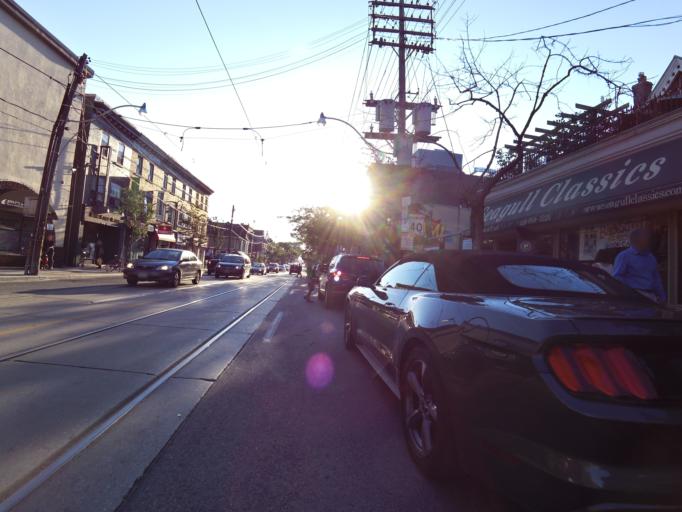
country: CA
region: Ontario
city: Scarborough
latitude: 43.6698
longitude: -79.3012
